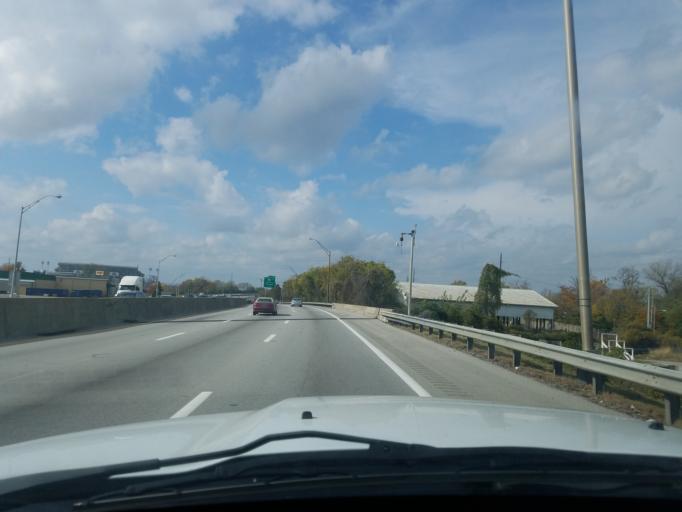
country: US
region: Kentucky
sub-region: Jefferson County
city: Audubon Park
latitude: 38.2062
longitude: -85.7444
